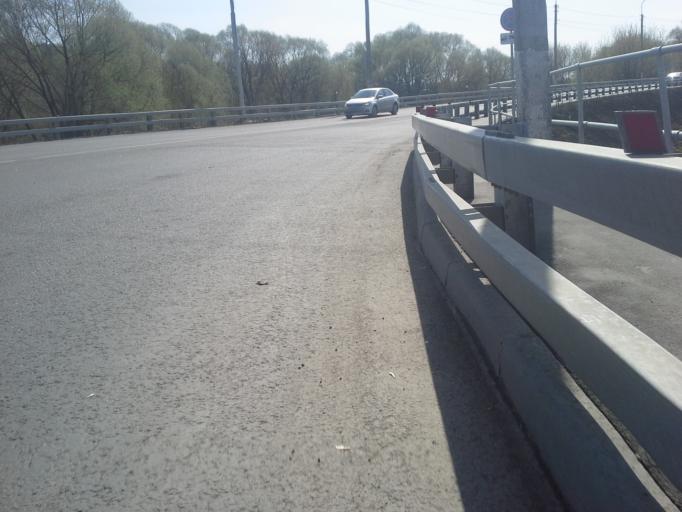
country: RU
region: Moskovskaya
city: Dubrovitsy
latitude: 55.4886
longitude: 37.5074
